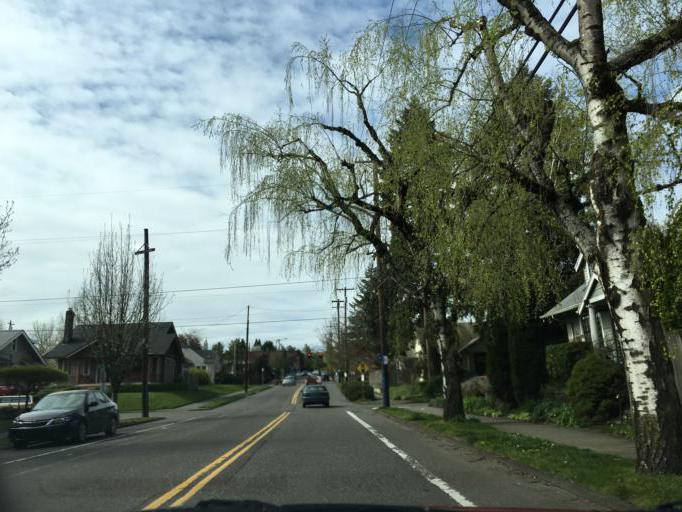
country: US
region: Oregon
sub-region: Clackamas County
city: Milwaukie
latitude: 45.4739
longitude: -122.6462
